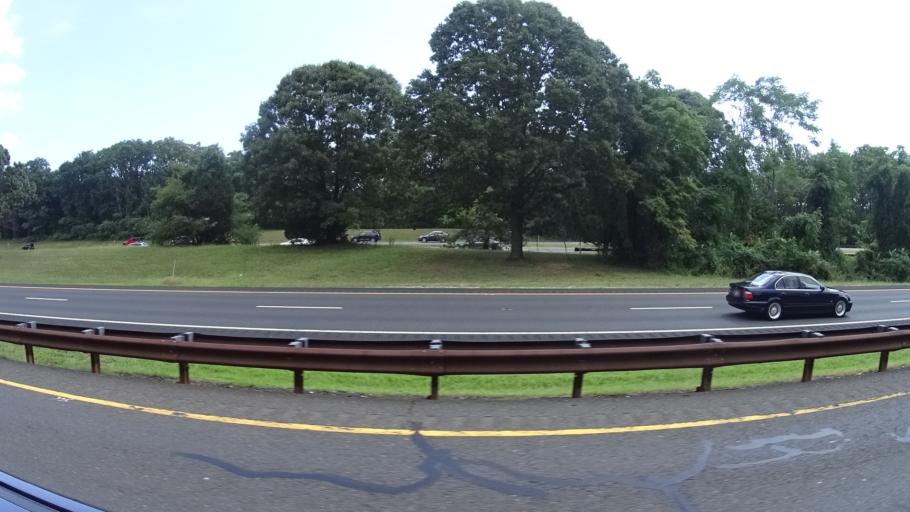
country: US
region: New Jersey
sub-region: Monmouth County
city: Lincroft
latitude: 40.3305
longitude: -74.0989
